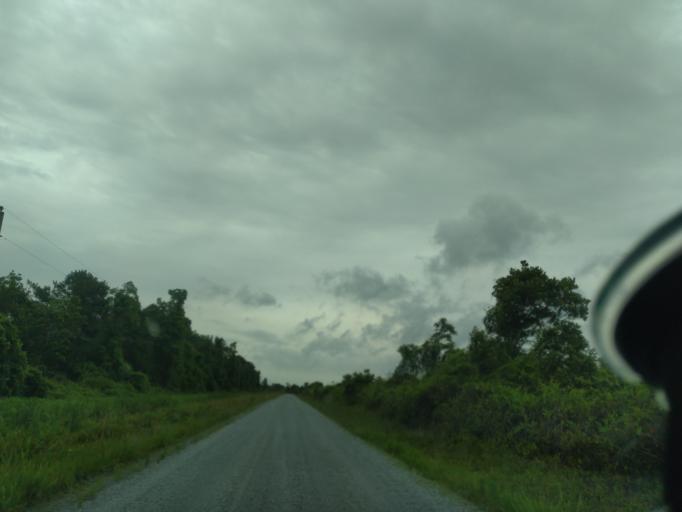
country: US
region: North Carolina
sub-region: Beaufort County
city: Belhaven
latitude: 35.7341
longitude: -76.4528
